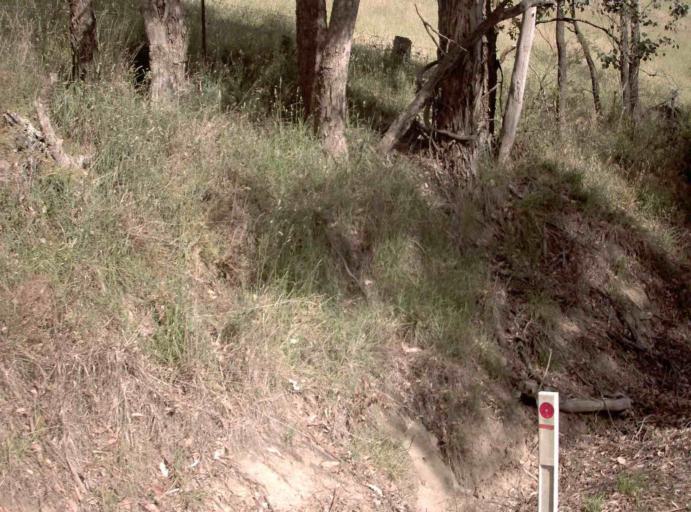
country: AU
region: Victoria
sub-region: East Gippsland
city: Lakes Entrance
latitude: -37.5159
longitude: 148.1415
